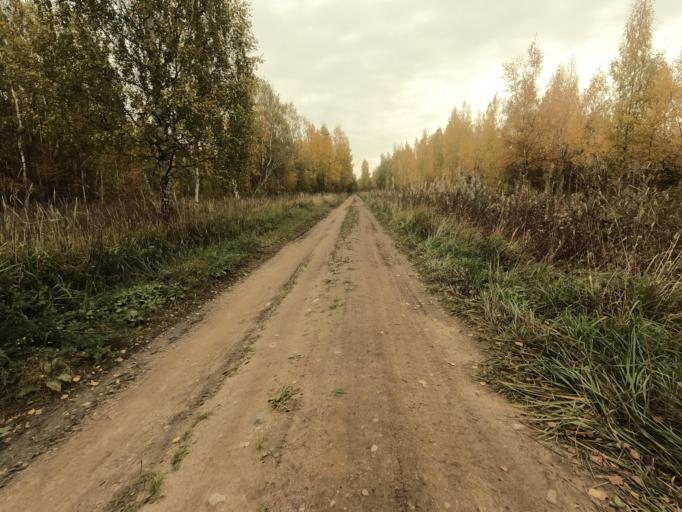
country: RU
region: Novgorod
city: Pankovka
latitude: 58.8660
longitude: 30.9260
